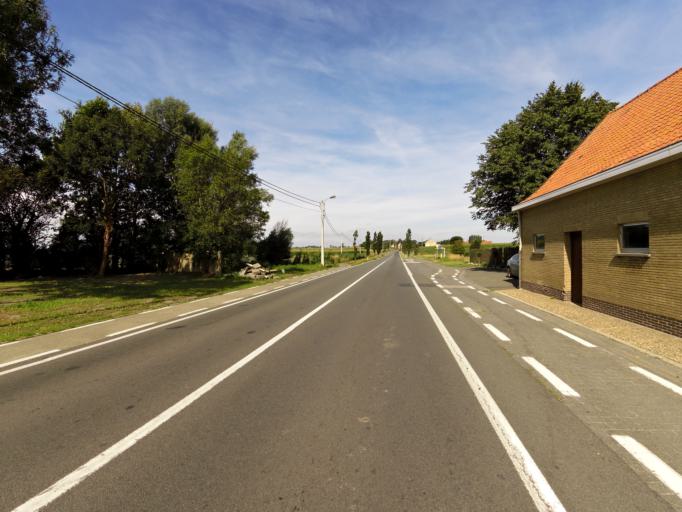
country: BE
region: Flanders
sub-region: Provincie West-Vlaanderen
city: Houthulst
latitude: 51.0194
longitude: 2.9397
